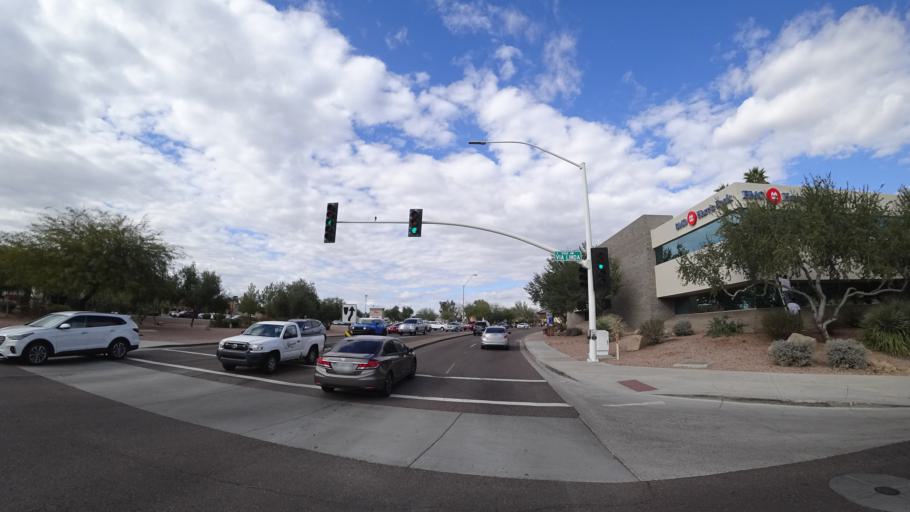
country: US
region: Arizona
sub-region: Maricopa County
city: Scottsdale
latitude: 33.5690
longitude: -111.8872
